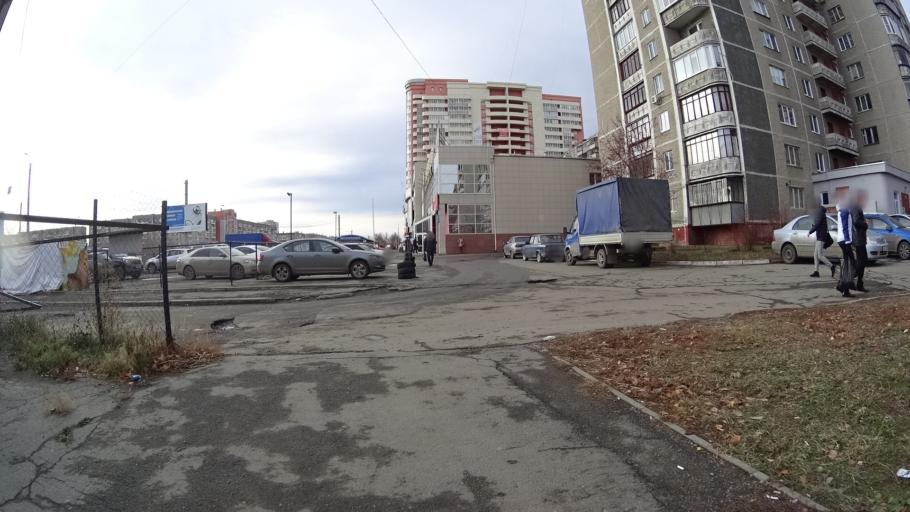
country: RU
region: Chelyabinsk
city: Roshchino
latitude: 55.1870
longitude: 61.3010
